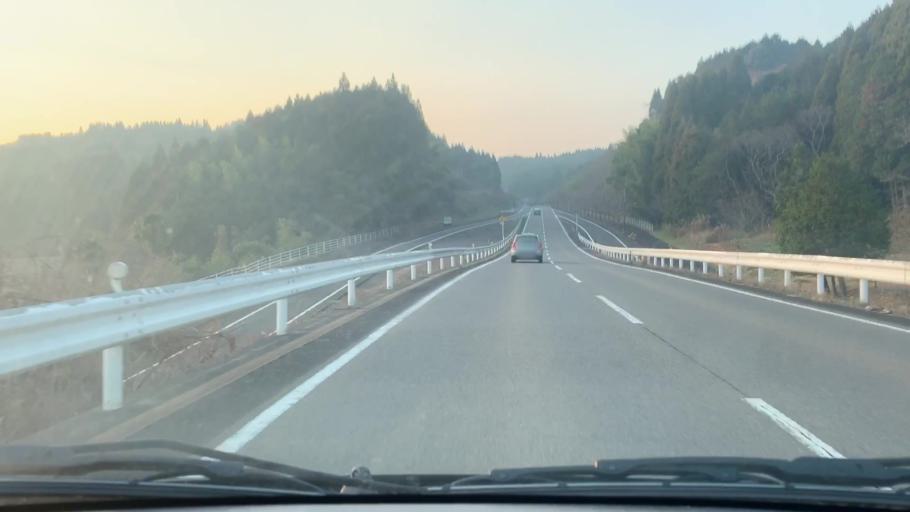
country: JP
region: Saga Prefecture
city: Imaricho-ko
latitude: 33.2645
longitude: 129.9594
